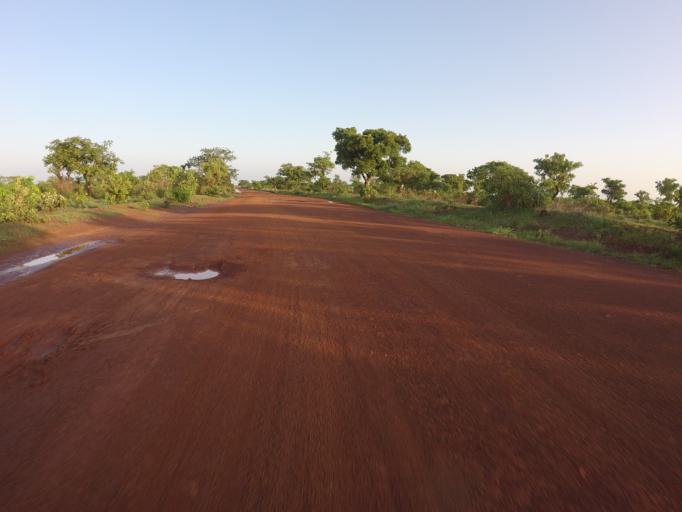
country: TG
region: Savanes
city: Sansanne-Mango
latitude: 10.2369
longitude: -0.0746
